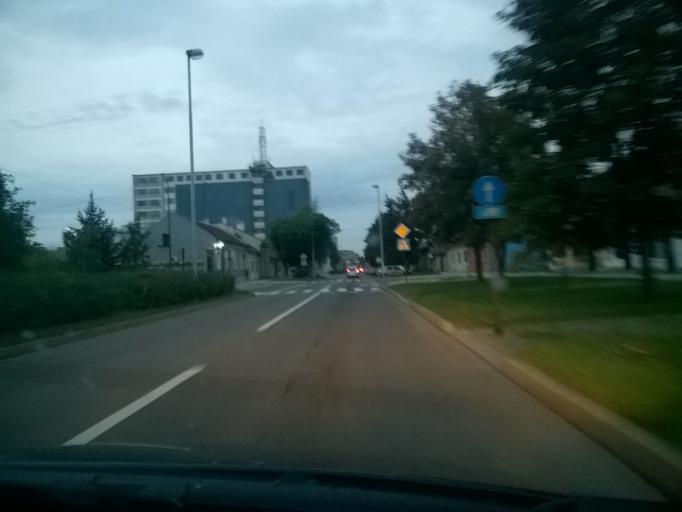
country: RS
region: Autonomna Pokrajina Vojvodina
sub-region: Juznobanatski Okrug
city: Pancevo
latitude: 44.8600
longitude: 20.6500
